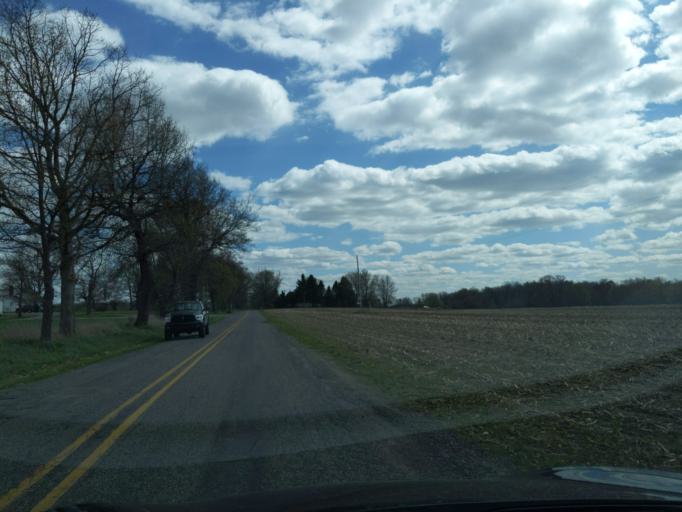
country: US
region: Michigan
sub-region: Ingham County
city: Leslie
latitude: 42.4869
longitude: -84.5412
